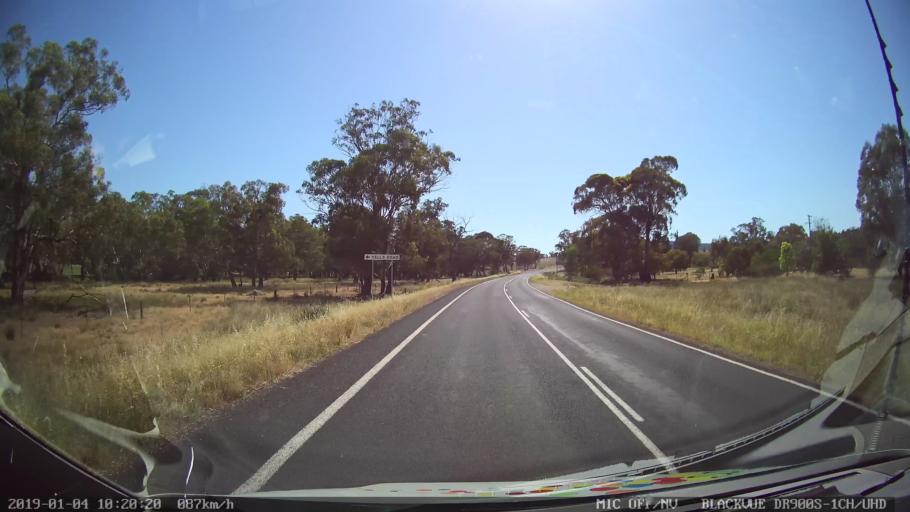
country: AU
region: New South Wales
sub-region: Cabonne
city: Canowindra
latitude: -33.3724
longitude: 148.4941
